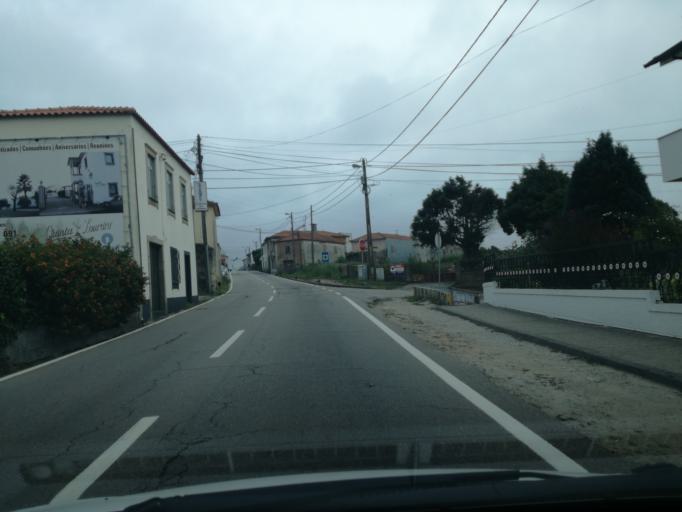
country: PT
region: Aveiro
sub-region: Espinho
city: Silvalde
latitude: 40.9977
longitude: -8.6357
